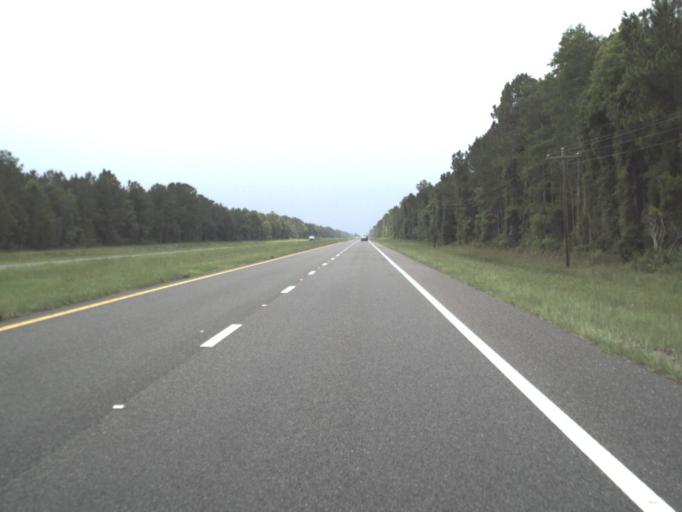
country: US
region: Florida
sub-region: Levy County
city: Chiefland
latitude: 29.3590
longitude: -82.7880
